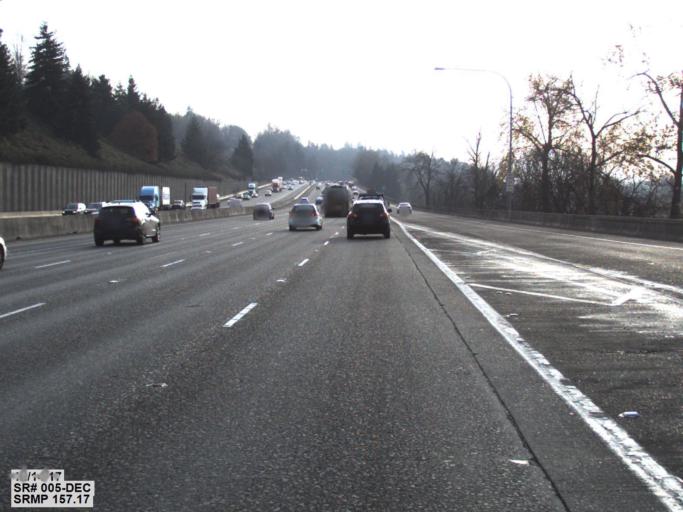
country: US
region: Washington
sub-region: King County
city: Tukwila
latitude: 47.4975
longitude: -122.2720
